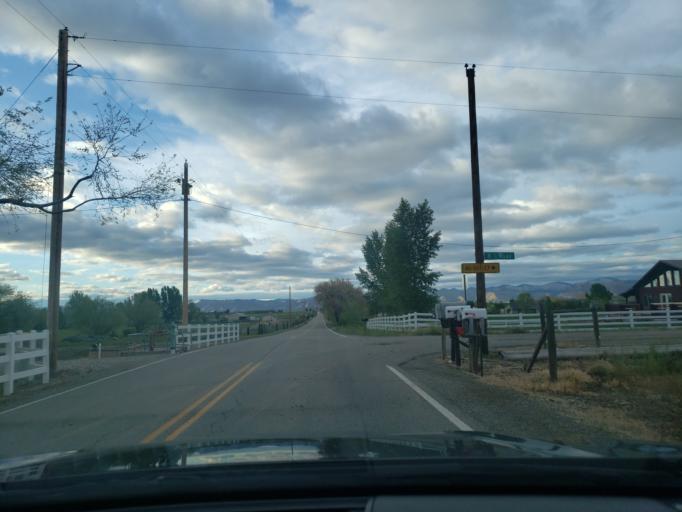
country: US
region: Colorado
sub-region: Mesa County
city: Fruita
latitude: 39.2146
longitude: -108.7197
